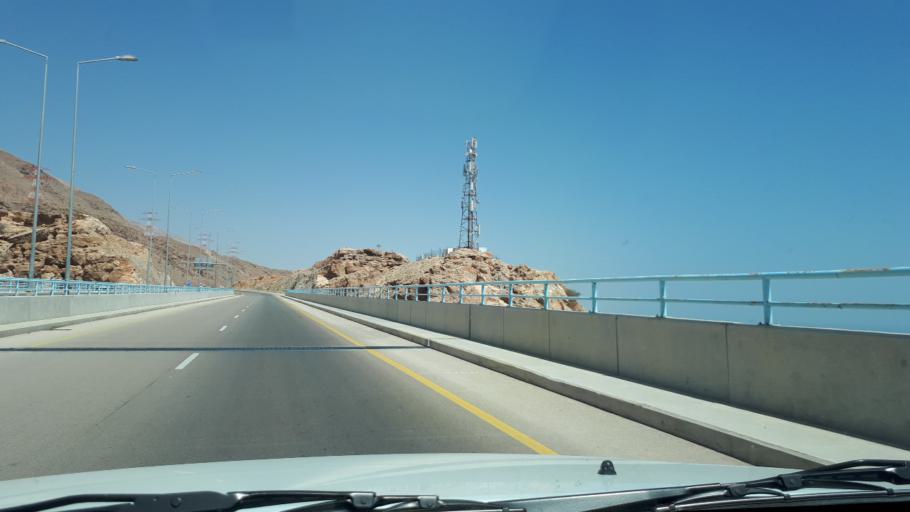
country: OM
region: Ash Sharqiyah
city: Sur
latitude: 22.8223
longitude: 59.2596
